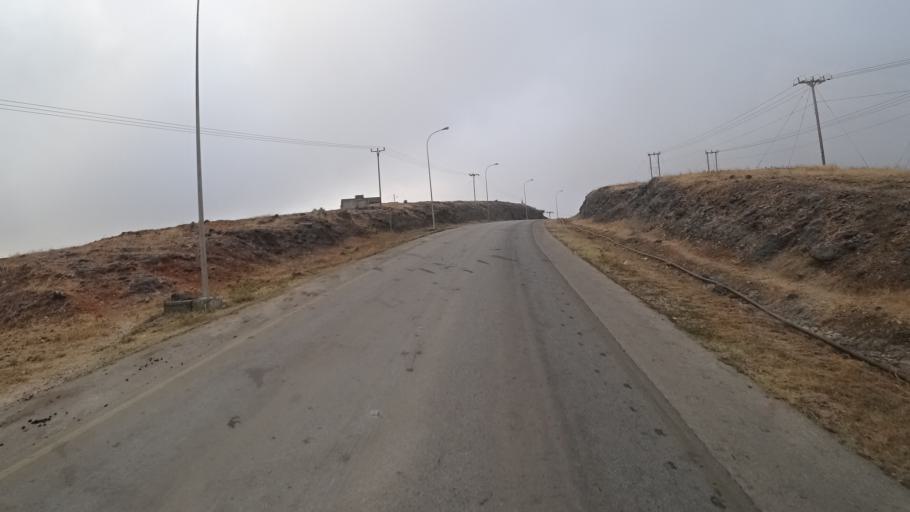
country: OM
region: Zufar
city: Salalah
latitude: 17.1225
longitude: 53.9759
